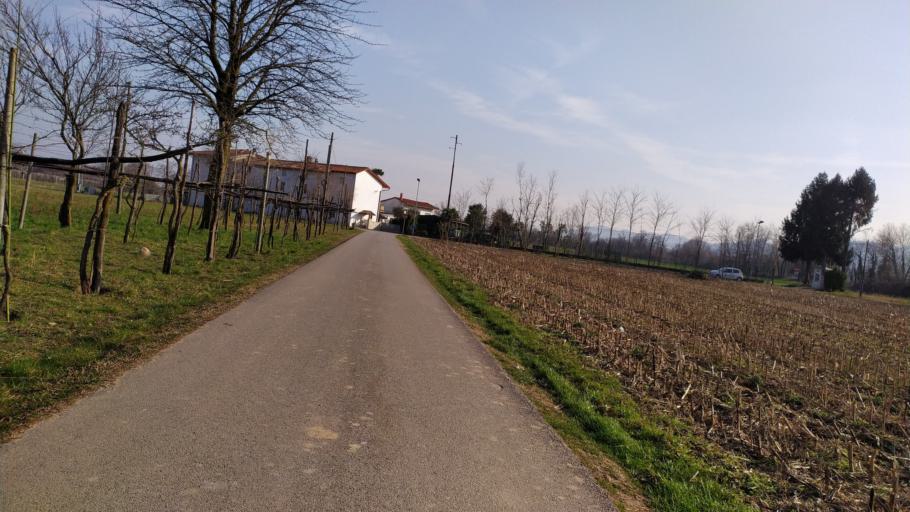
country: IT
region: Veneto
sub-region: Provincia di Vicenza
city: Giavenale
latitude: 45.6921
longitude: 11.4031
